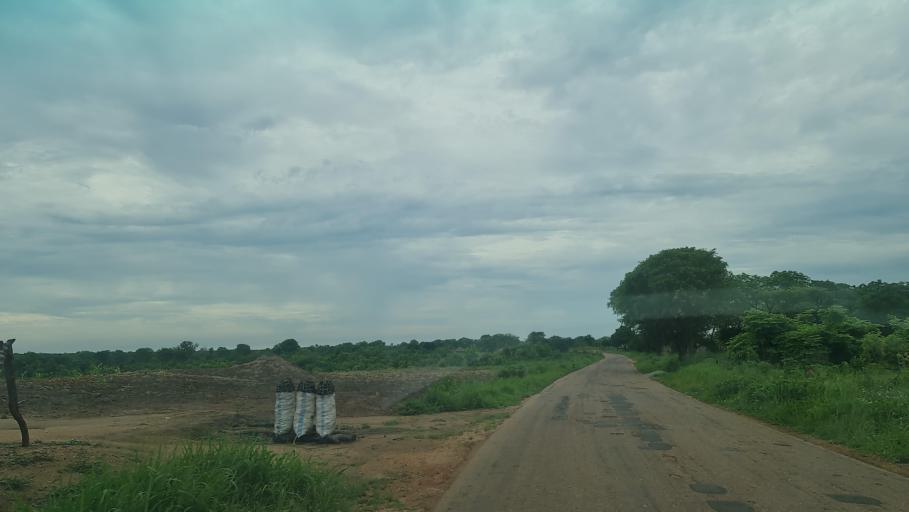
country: MW
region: Southern Region
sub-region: Nsanje District
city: Nsanje
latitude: -17.6903
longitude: 35.7336
